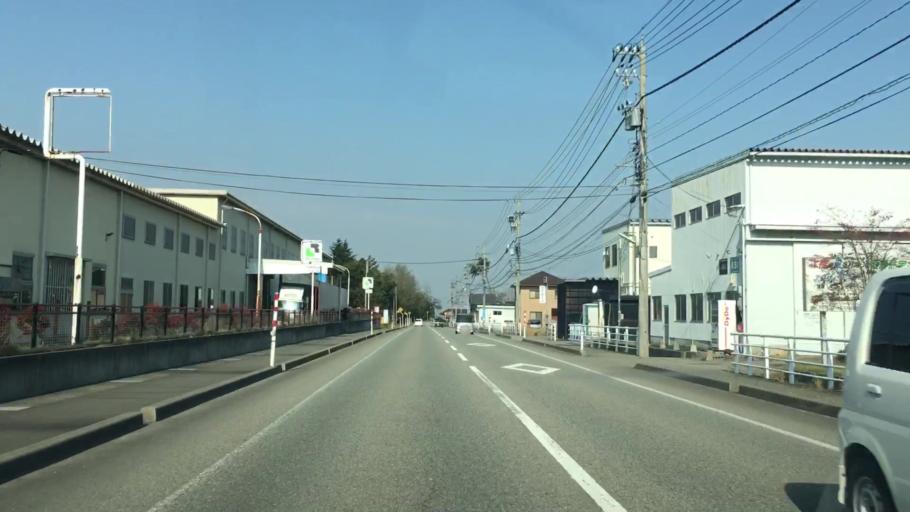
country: JP
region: Toyama
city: Yatsuomachi-higashikumisaka
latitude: 36.5881
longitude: 137.1909
